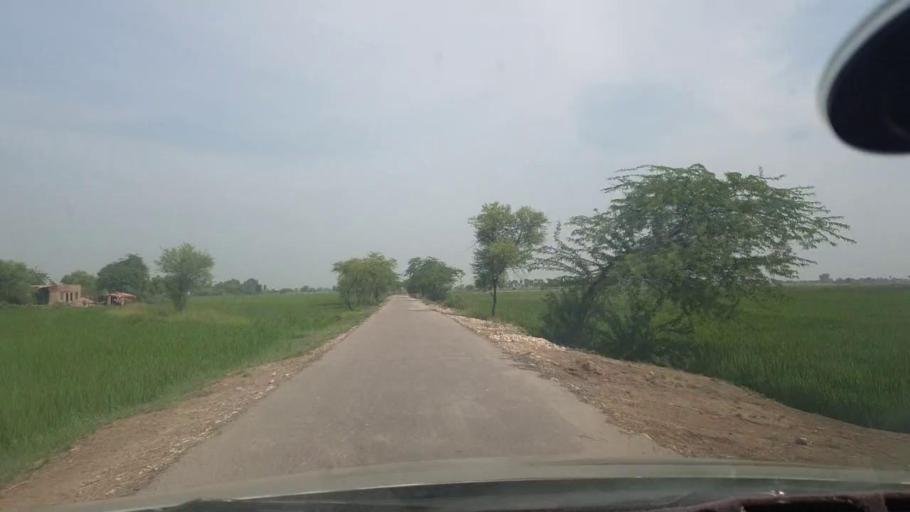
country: PK
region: Sindh
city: Jacobabad
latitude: 28.3031
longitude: 68.4749
